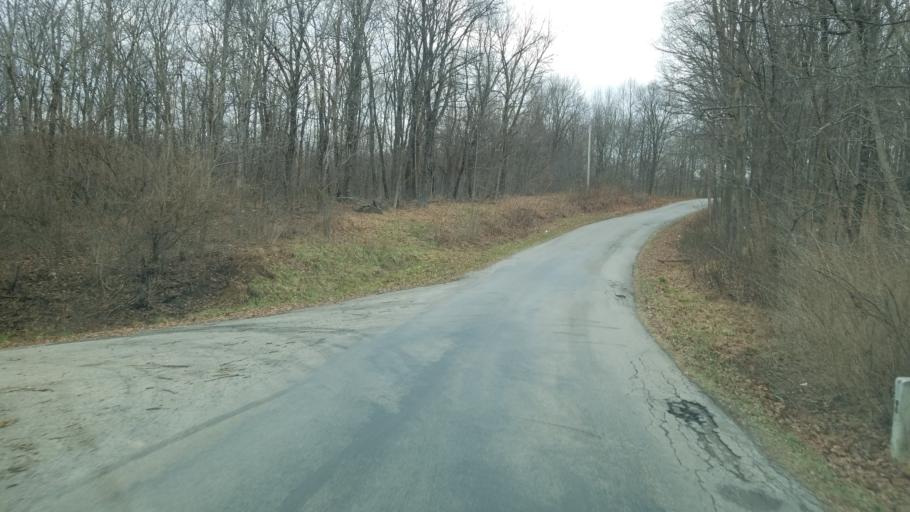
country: US
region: Ohio
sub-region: Highland County
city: Greenfield
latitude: 39.1857
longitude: -83.2666
